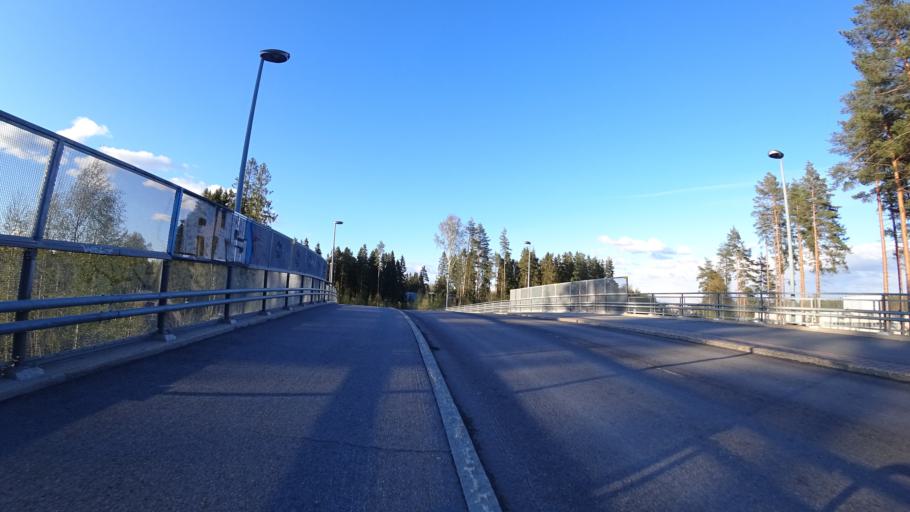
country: FI
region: Pirkanmaa
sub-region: Tampere
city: Pirkkala
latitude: 61.5015
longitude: 23.6104
